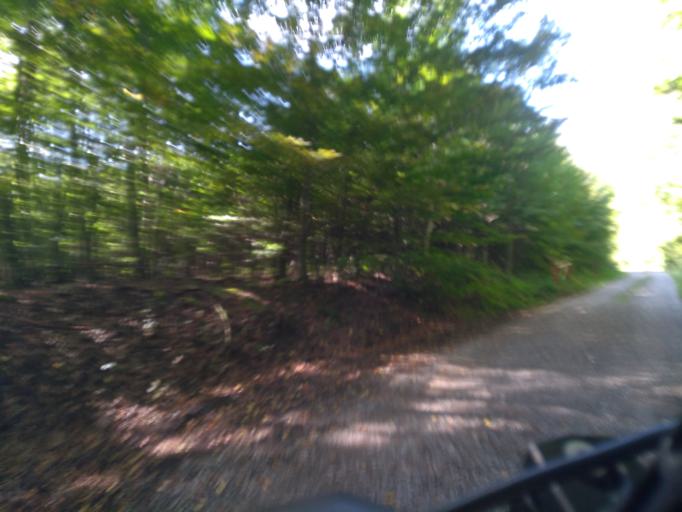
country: DE
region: Baden-Wuerttemberg
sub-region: Karlsruhe Region
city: Ispringen
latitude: 48.9096
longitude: 8.6270
